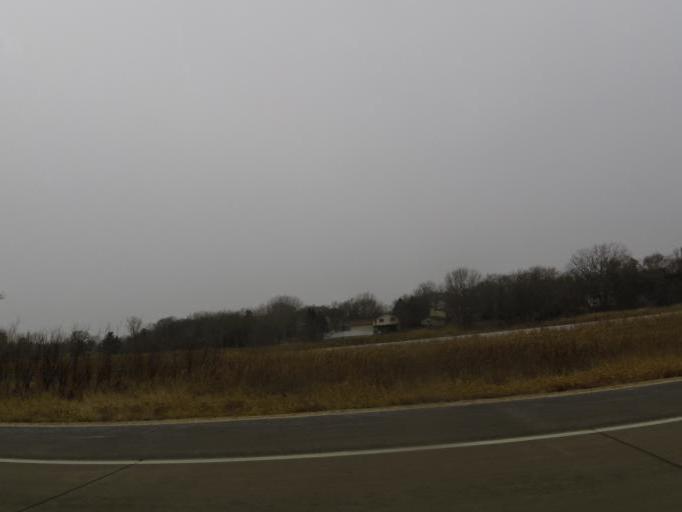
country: US
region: Minnesota
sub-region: Washington County
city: Oakdale
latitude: 44.9684
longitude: -92.9586
